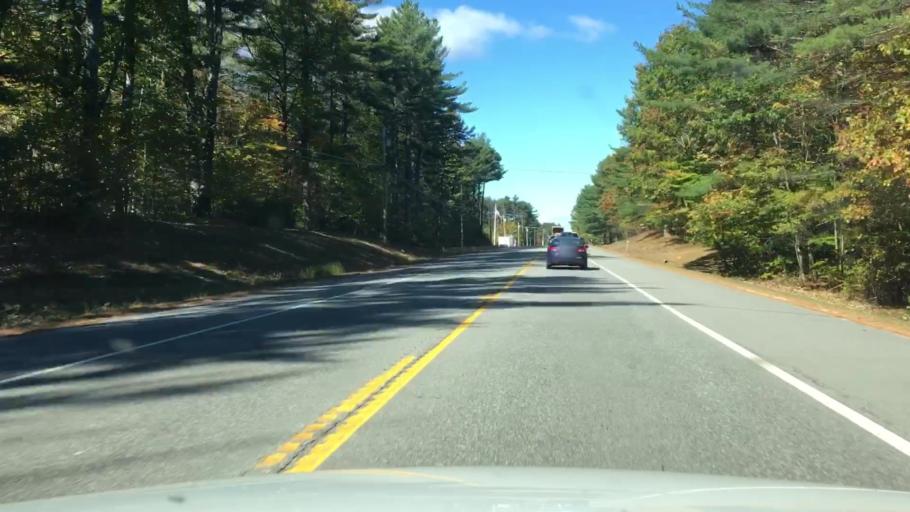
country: US
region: New Hampshire
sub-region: Carroll County
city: Ossipee
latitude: 43.6888
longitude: -71.0941
